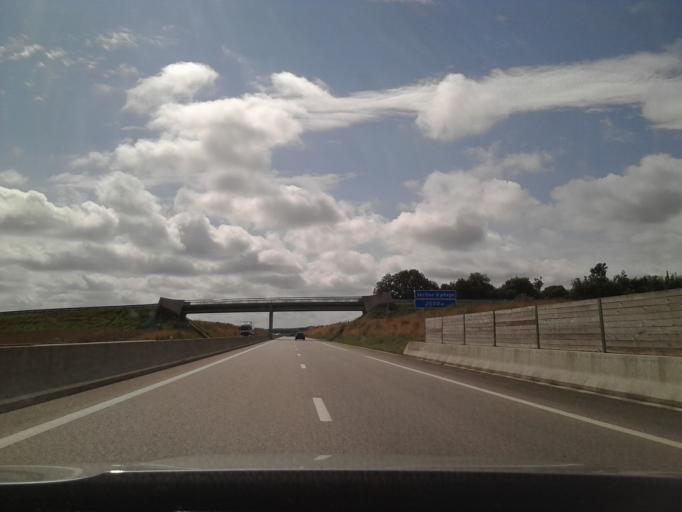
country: FR
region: Lower Normandy
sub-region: Departement du Calvados
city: Falaise
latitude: 48.8711
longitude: -0.2098
